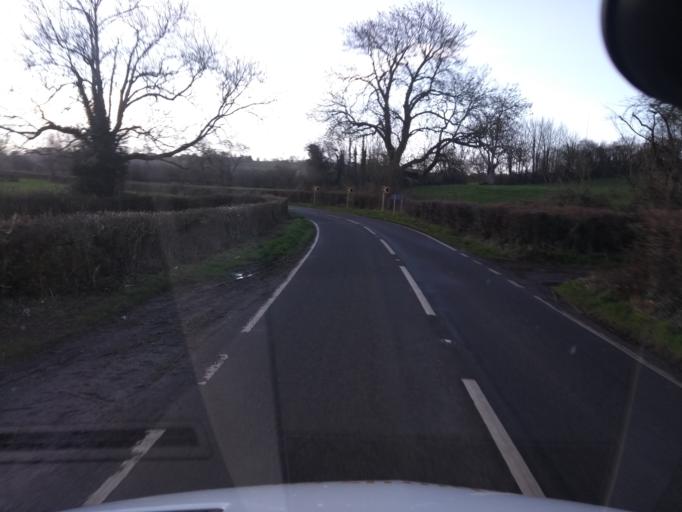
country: GB
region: England
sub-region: Somerset
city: Wedmore
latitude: 51.2180
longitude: -2.7881
